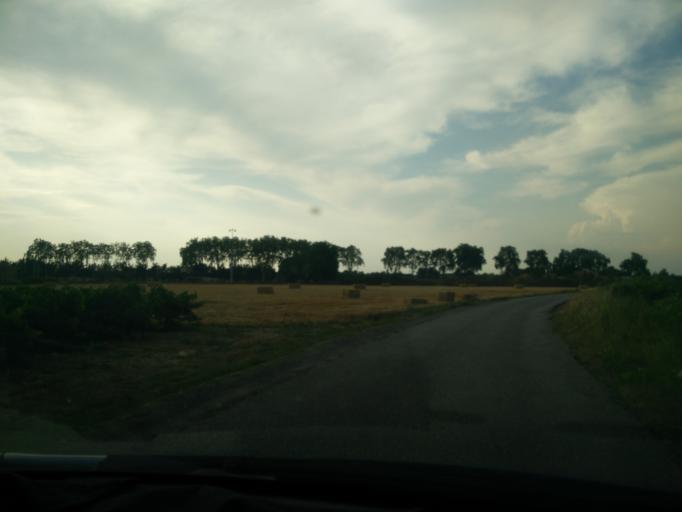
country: FR
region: Languedoc-Roussillon
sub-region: Departement de l'Herault
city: Marsillargues
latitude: 43.6875
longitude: 4.1621
